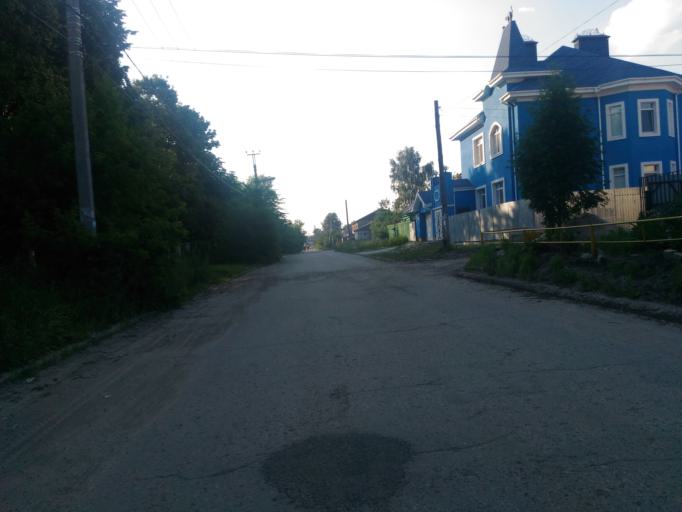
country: RU
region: Ulyanovsk
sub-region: Ulyanovskiy Rayon
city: Ulyanovsk
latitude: 54.3348
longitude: 48.3673
